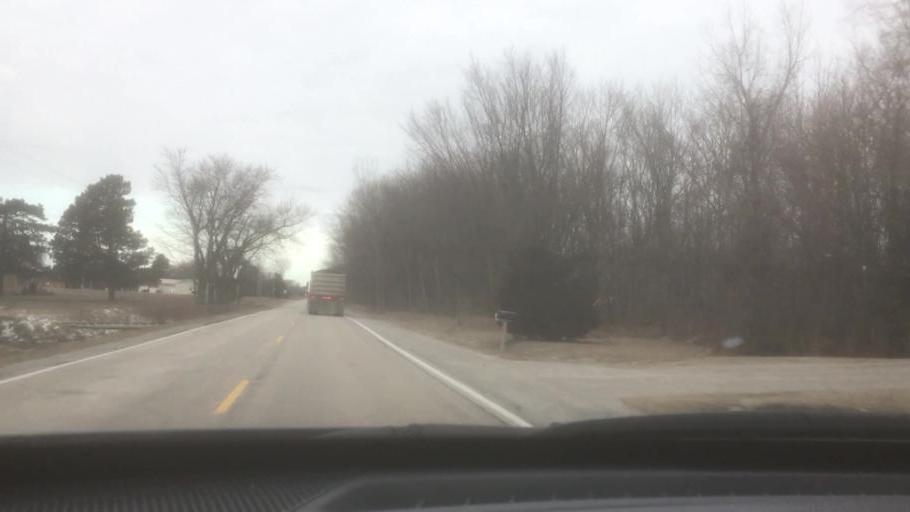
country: US
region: Michigan
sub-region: Bay County
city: Essexville
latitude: 43.5221
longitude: -83.7943
